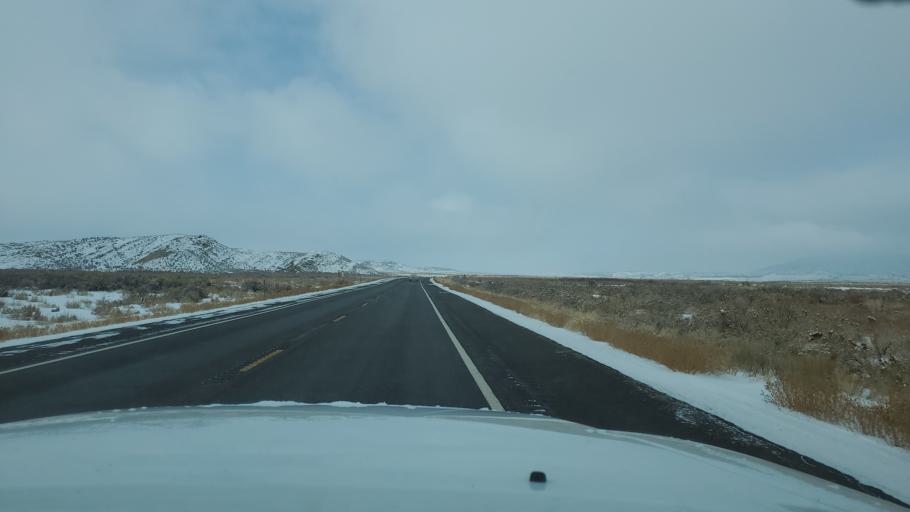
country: US
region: Utah
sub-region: Uintah County
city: Naples
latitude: 40.2875
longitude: -109.1464
